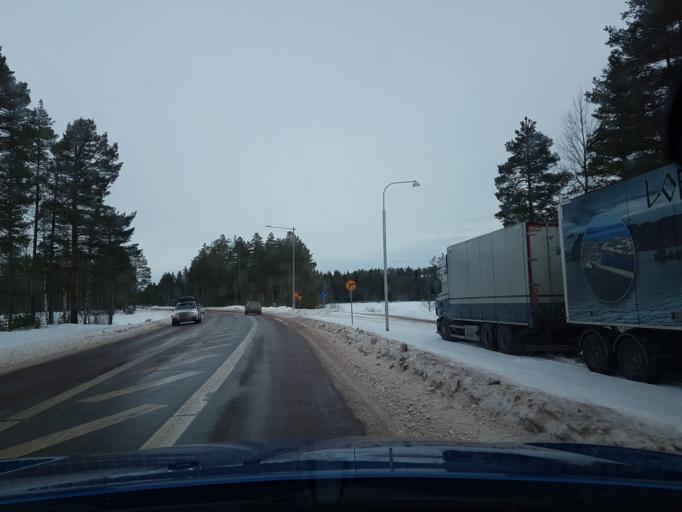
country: SE
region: Dalarna
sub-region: Orsa Kommun
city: Orsa
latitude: 61.6005
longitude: 14.8228
